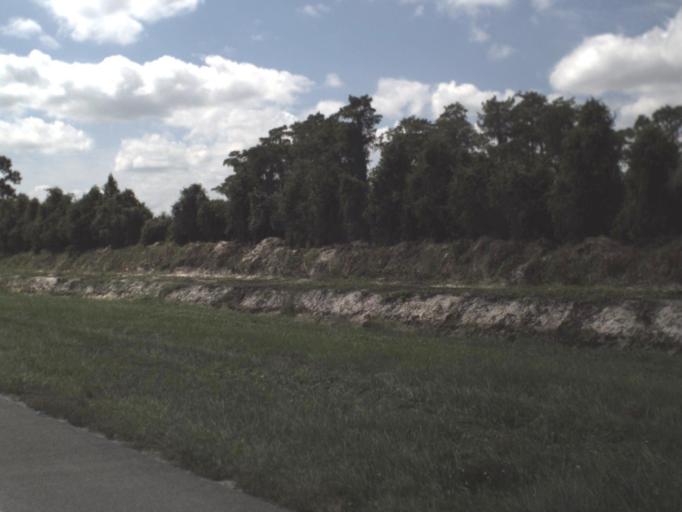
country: US
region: Florida
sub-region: Hendry County
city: LaBelle
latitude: 26.6941
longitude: -81.4370
